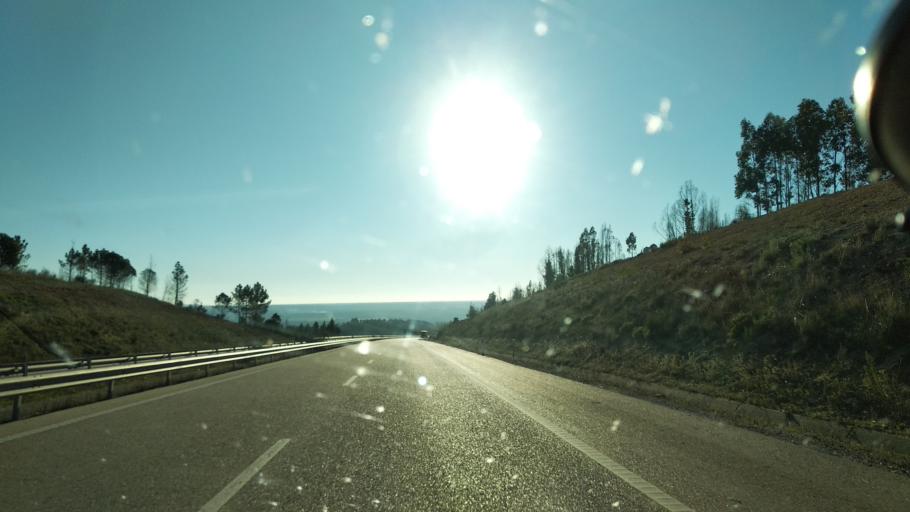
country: PT
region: Santarem
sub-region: Macao
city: Macao
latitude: 39.5056
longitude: -8.0232
